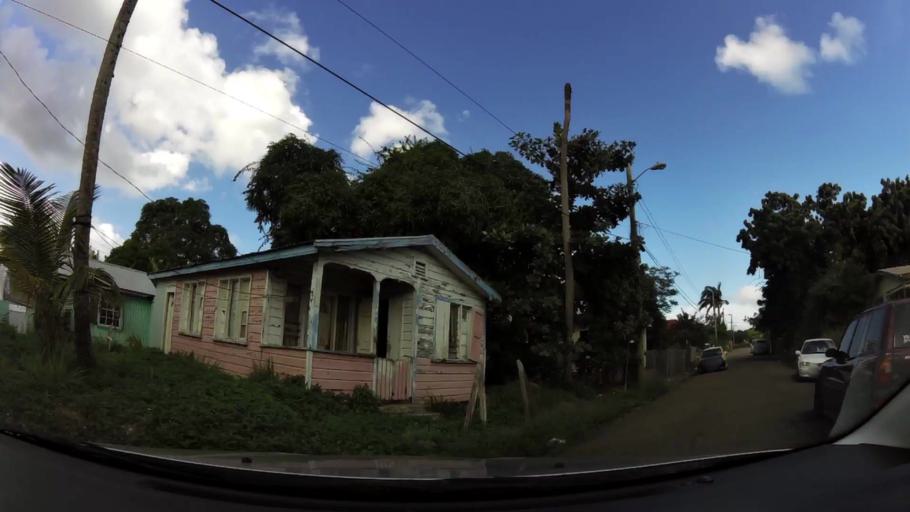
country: AG
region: Saint John
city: Saint John's
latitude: 17.1073
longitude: -61.8373
